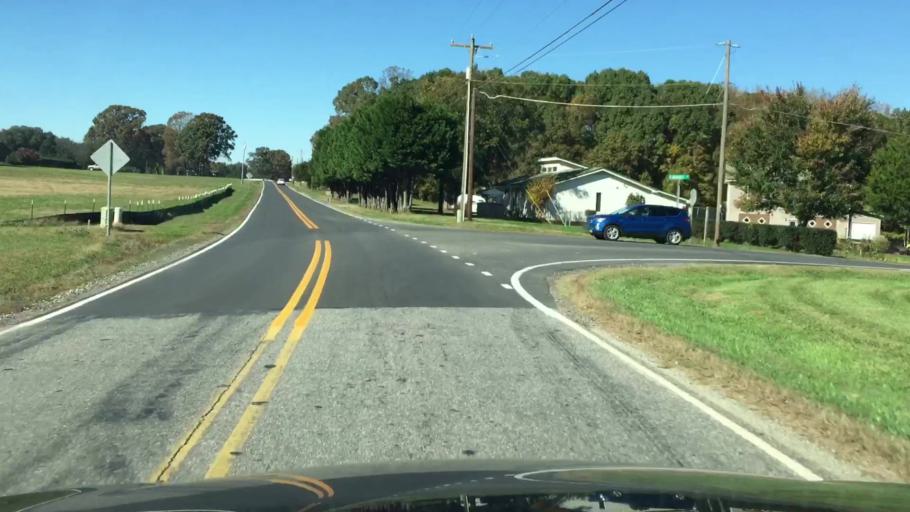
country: US
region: North Carolina
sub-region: Iredell County
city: Mooresville
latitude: 35.5679
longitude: -80.7754
